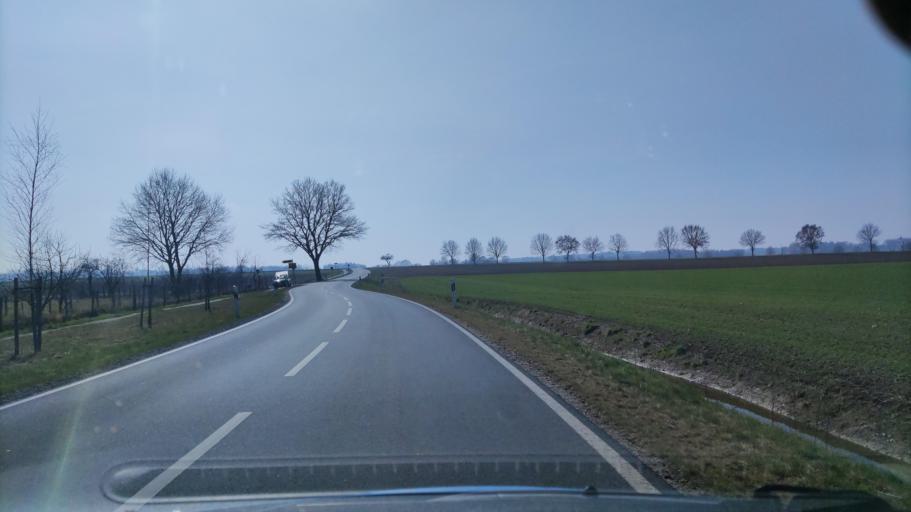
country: DE
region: Lower Saxony
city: Clenze
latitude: 52.9652
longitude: 10.9721
